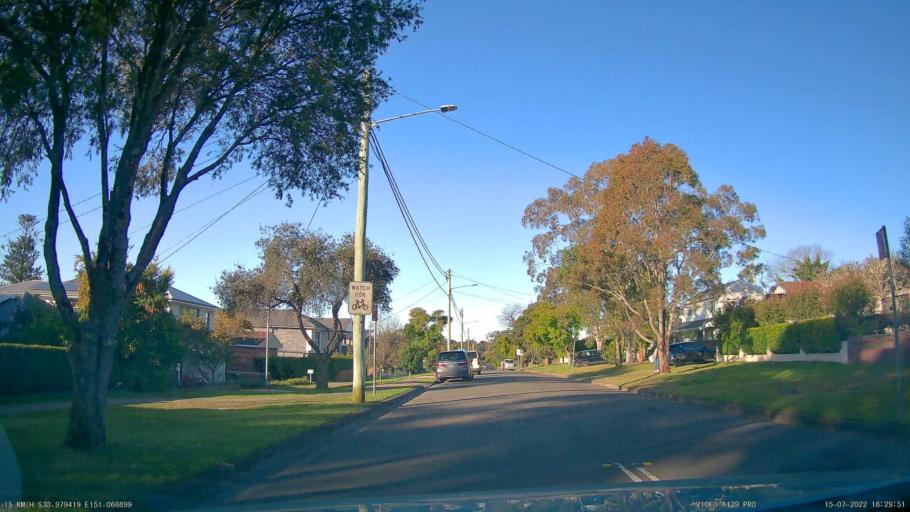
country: AU
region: New South Wales
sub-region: Hurstville
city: Oatley
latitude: -33.9794
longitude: 151.0669
